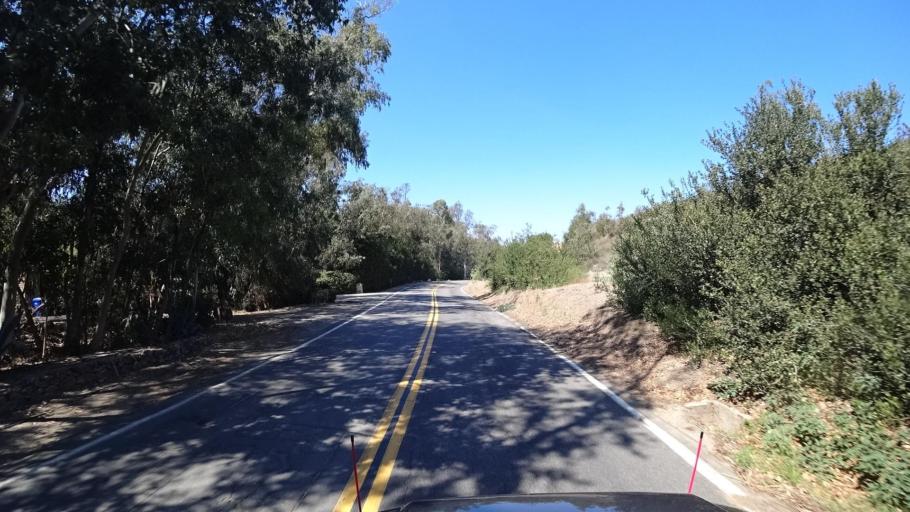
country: US
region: California
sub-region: San Diego County
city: Rancho Santa Fe
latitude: 33.0092
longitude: -117.2266
